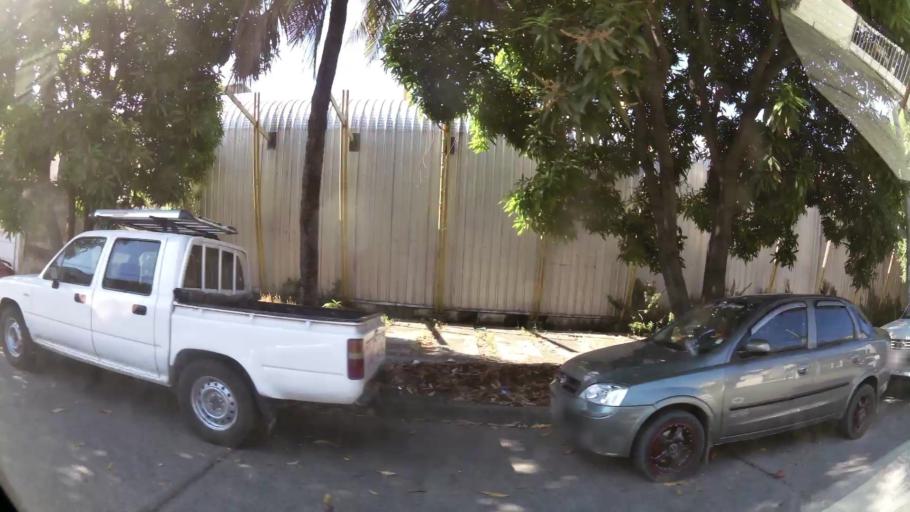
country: EC
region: Guayas
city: Eloy Alfaro
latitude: -2.1475
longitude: -79.9028
